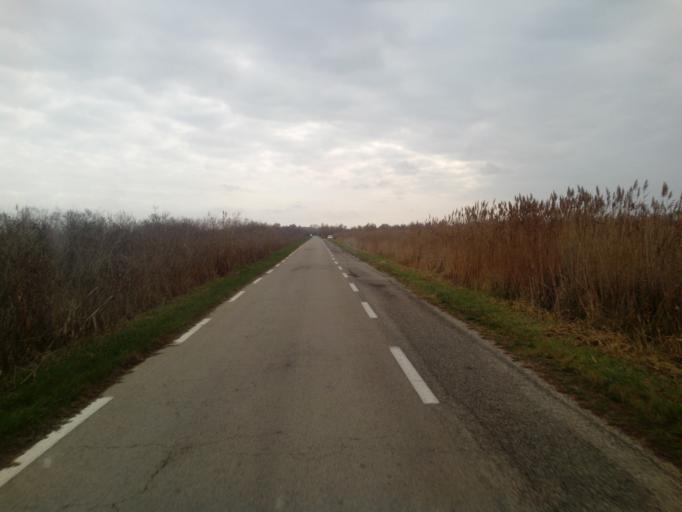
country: FR
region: Languedoc-Roussillon
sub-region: Departement du Gard
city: Vauvert
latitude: 43.6113
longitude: 4.3299
